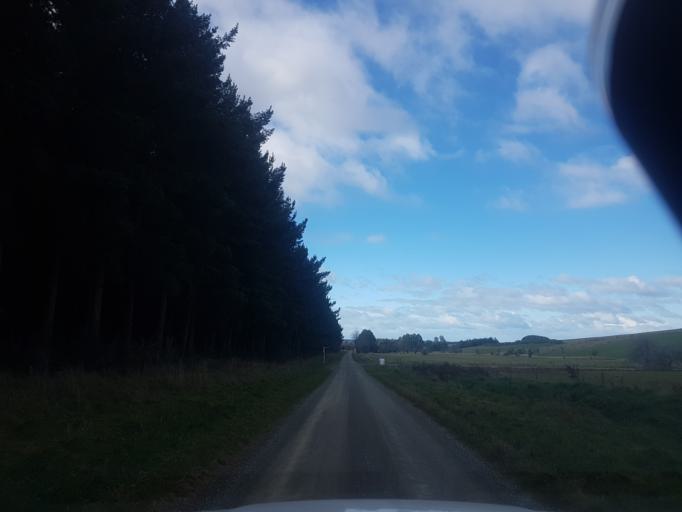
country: NZ
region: Canterbury
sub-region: Timaru District
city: Pleasant Point
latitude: -44.1879
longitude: 171.1620
